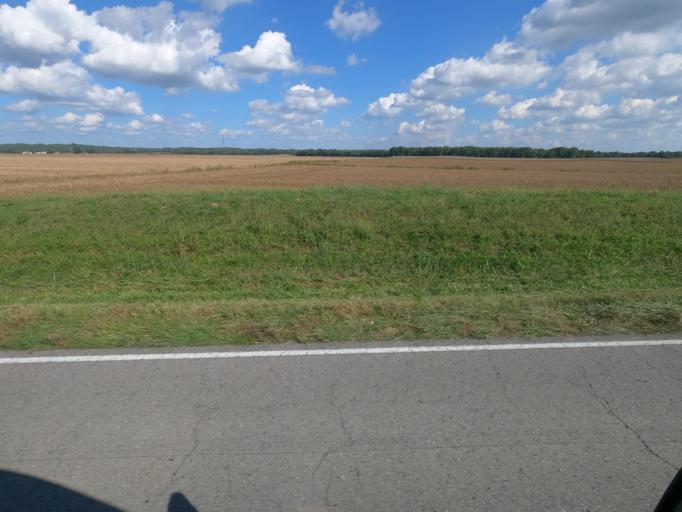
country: US
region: Illinois
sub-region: Massac County
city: Metropolis
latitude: 37.2643
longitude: -88.7614
